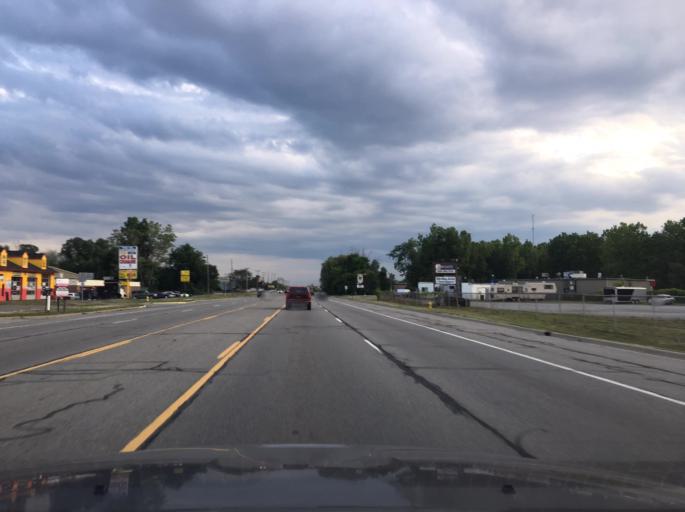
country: US
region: Michigan
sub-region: Macomb County
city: Clinton
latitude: 42.5612
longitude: -82.9185
